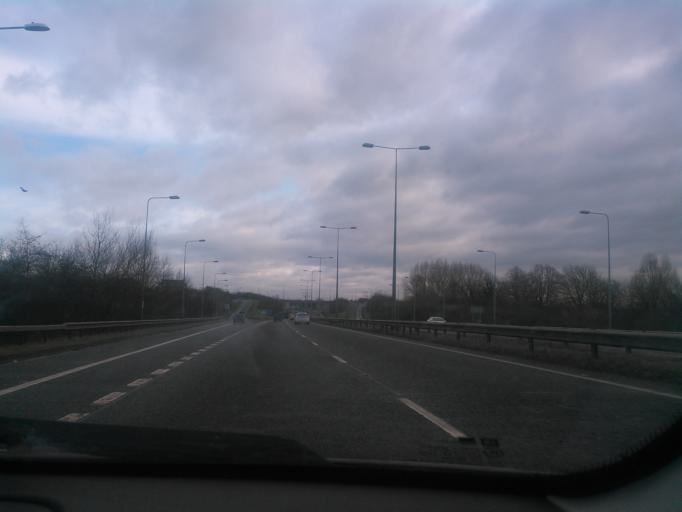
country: GB
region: England
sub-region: Derbyshire
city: Melbourne
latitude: 52.8620
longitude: -1.4476
